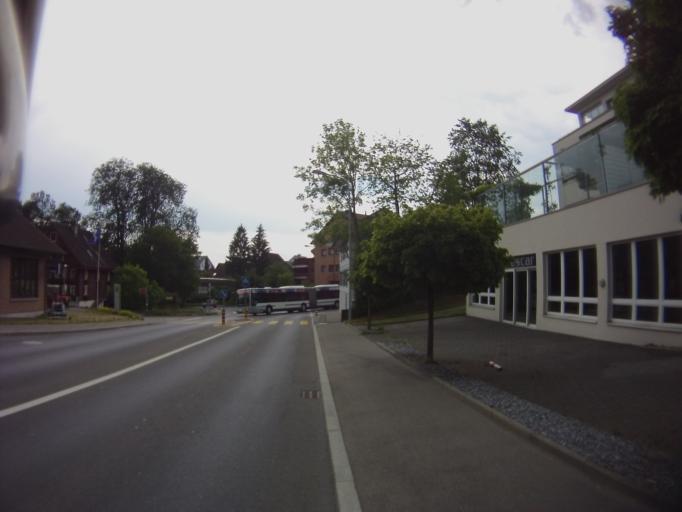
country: CH
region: Zug
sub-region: Zug
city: Hunenberg
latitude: 47.1721
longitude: 8.4265
